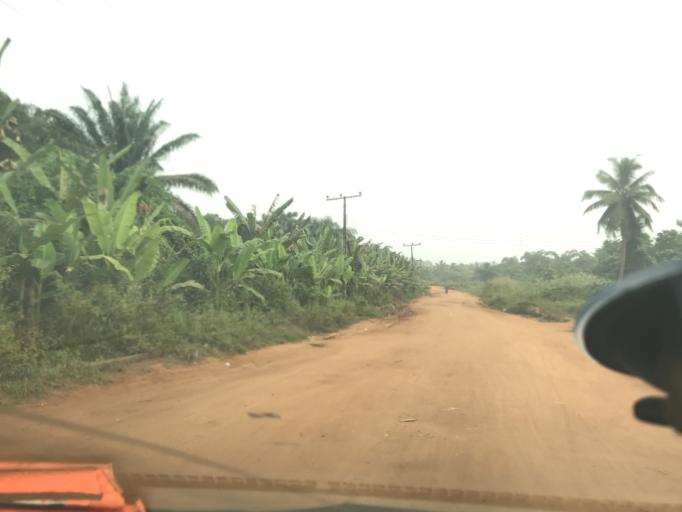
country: NG
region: Ogun
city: Ado Odo
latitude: 6.5835
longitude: 2.9321
